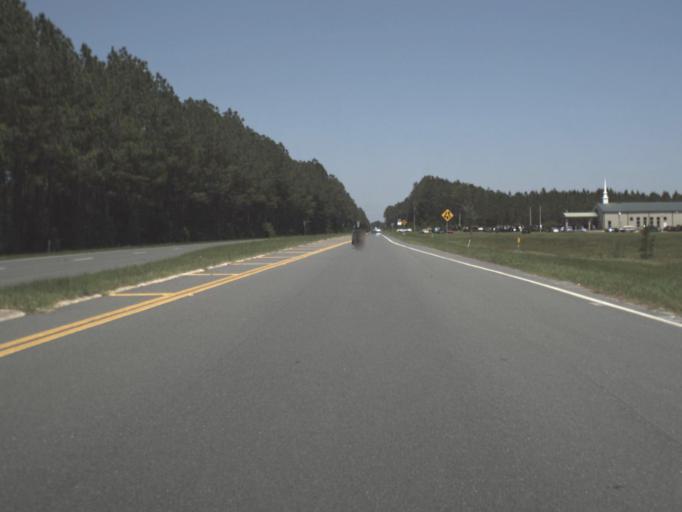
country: US
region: Florida
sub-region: Baker County
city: Macclenny
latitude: 30.2399
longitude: -82.3007
